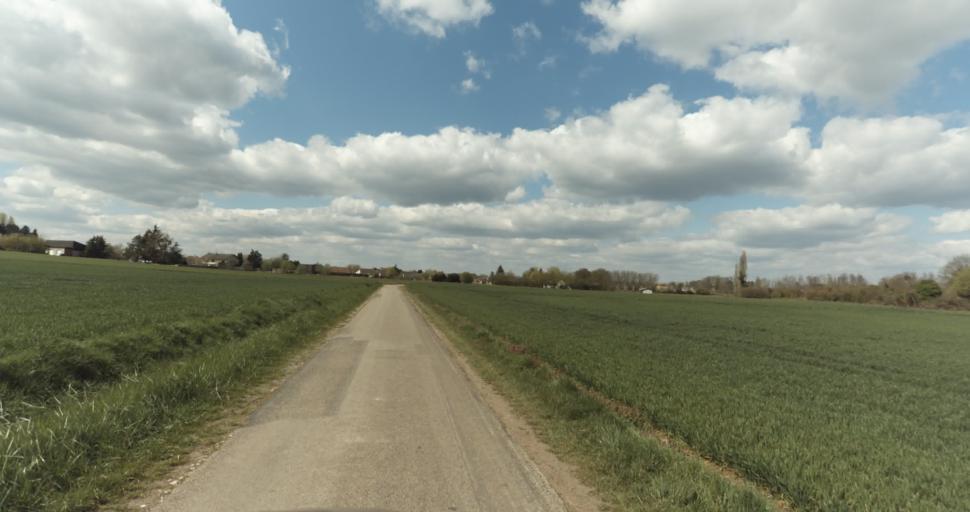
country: FR
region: Bourgogne
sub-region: Departement de la Cote-d'Or
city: Auxonne
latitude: 47.1869
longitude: 5.4110
